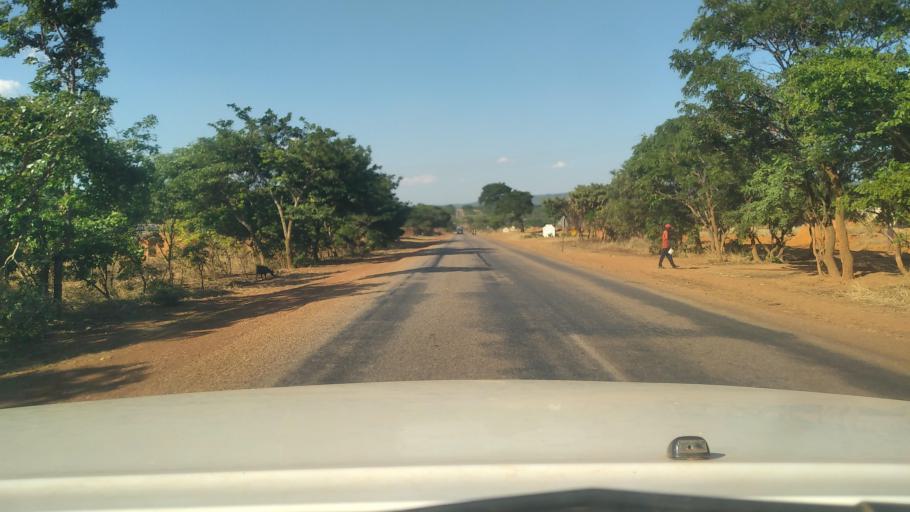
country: ZM
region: Northern
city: Mpika
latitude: -11.7471
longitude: 31.4658
